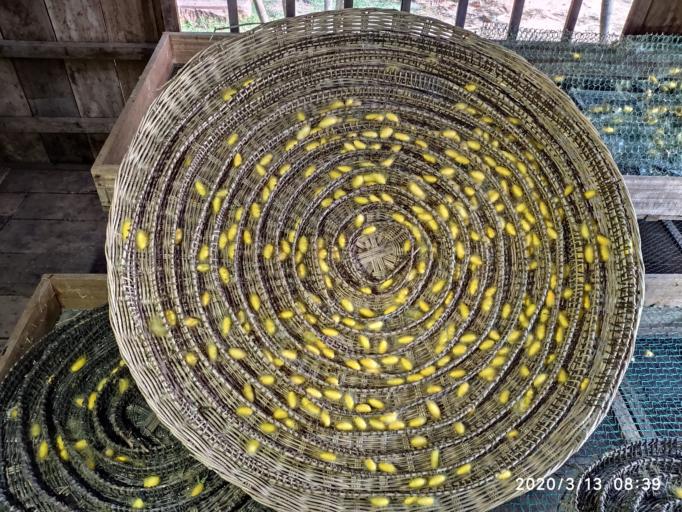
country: KH
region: Siem Reap
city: Siem Reap
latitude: 13.4371
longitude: 103.7457
